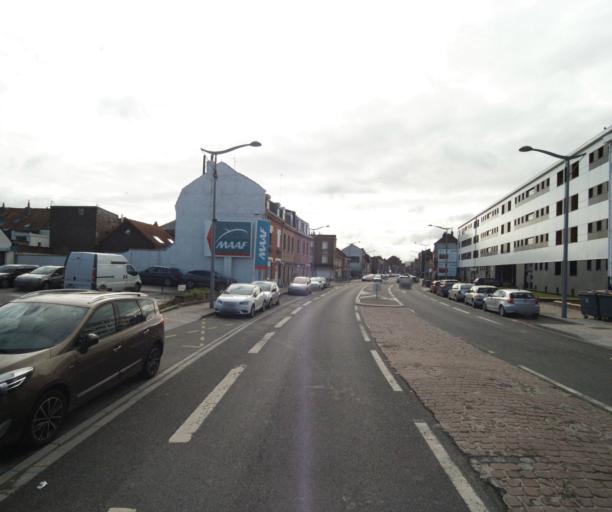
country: FR
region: Nord-Pas-de-Calais
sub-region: Departement du Nord
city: Lambersart
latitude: 50.6442
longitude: 3.0144
